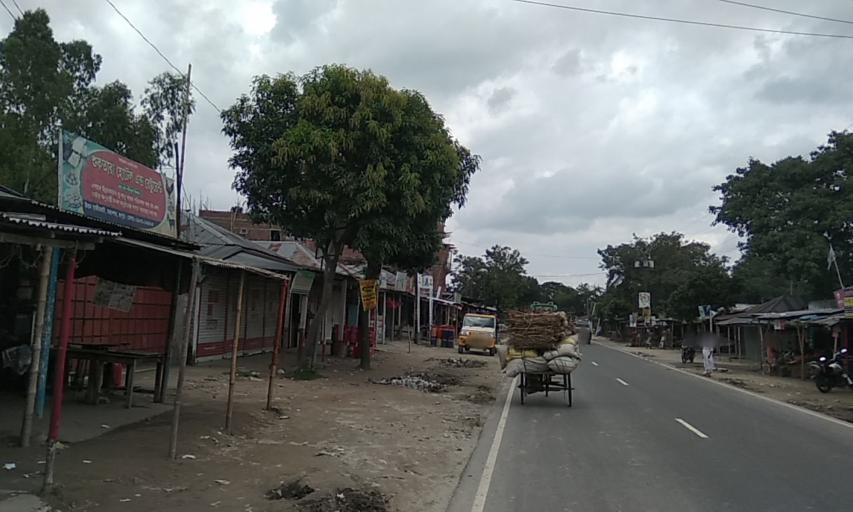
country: BD
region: Rangpur Division
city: Rangpur
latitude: 25.7989
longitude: 89.1923
